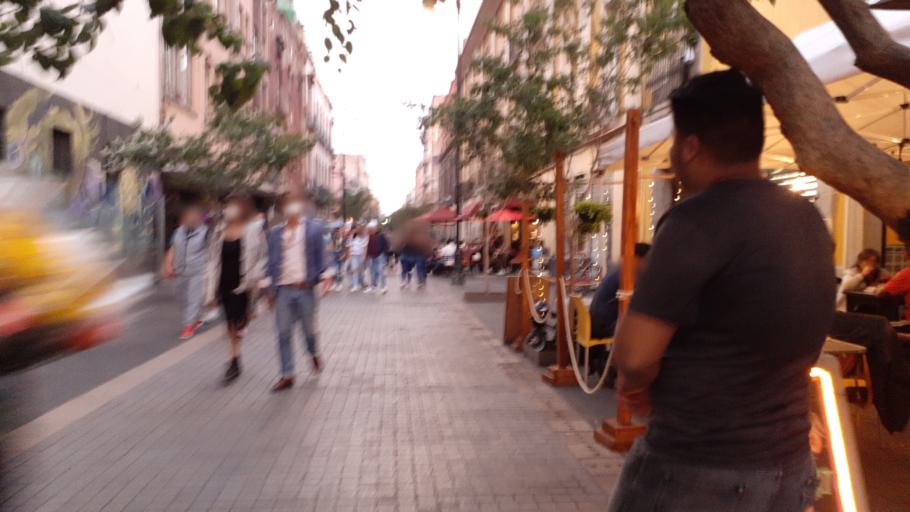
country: MX
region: Mexico City
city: Mexico City
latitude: 19.4277
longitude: -99.1358
